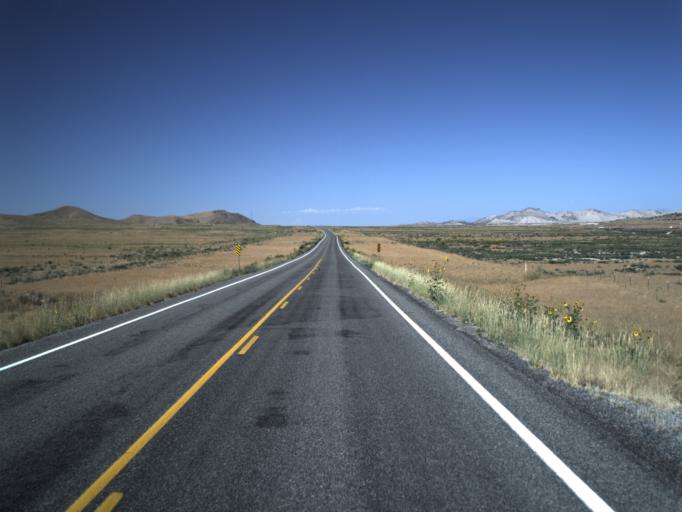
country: US
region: Utah
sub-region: Juab County
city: Nephi
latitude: 39.6818
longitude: -112.2498
